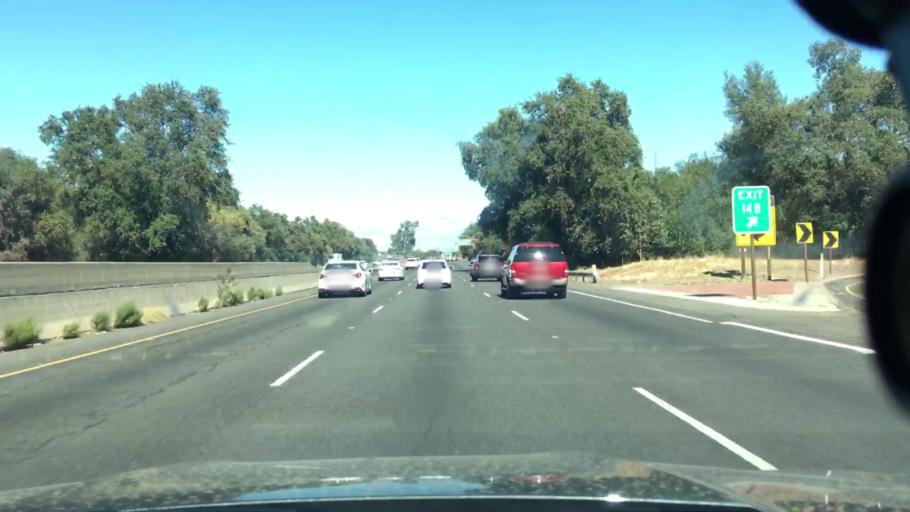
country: US
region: California
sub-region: Sacramento County
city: Arden-Arcade
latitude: 38.6403
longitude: -121.3826
